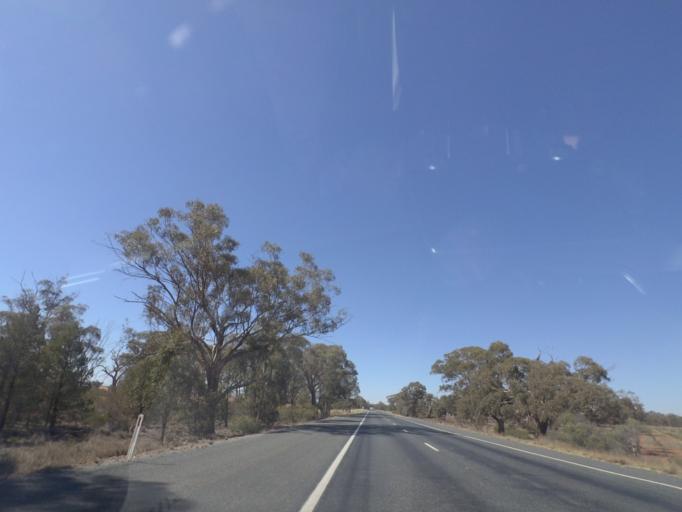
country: AU
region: New South Wales
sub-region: Bland
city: West Wyalong
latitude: -34.1943
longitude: 147.1112
